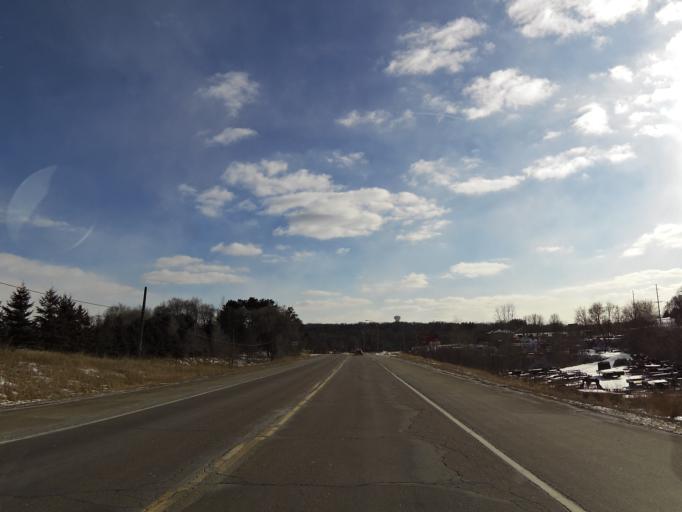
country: US
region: Minnesota
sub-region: Dakota County
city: Eagan
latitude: 44.8121
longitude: -93.1003
